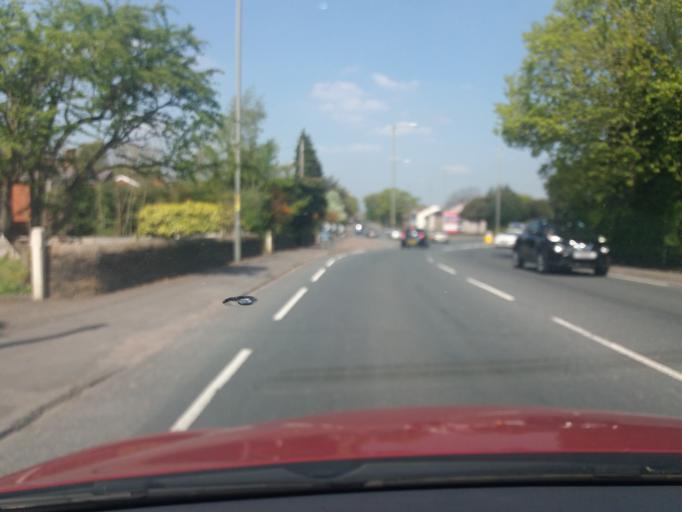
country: GB
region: England
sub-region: Lancashire
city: Chorley
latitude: 53.6771
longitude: -2.6354
